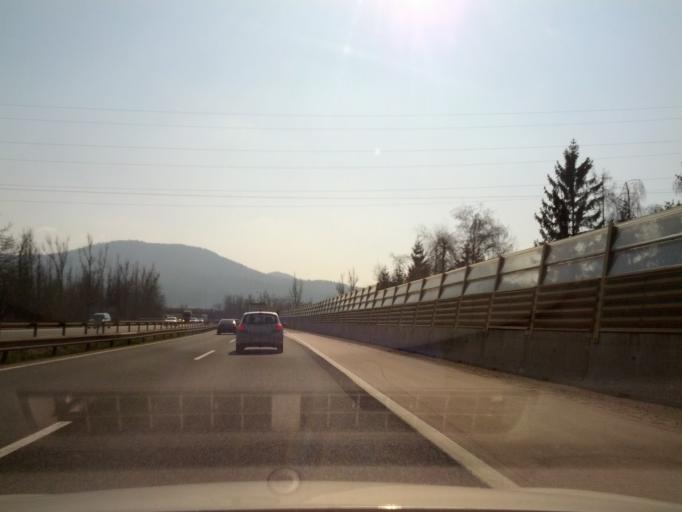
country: SI
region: Vrhnika
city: Vrhnika
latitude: 45.9726
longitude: 14.3059
